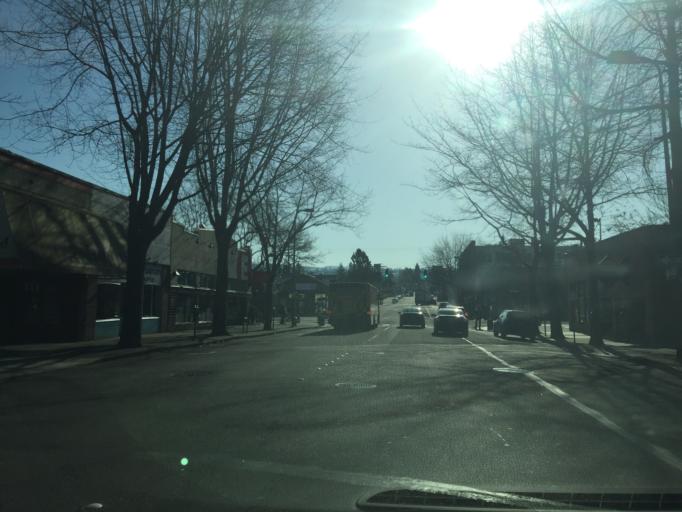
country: US
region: Washington
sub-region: Whatcom County
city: Bellingham
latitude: 48.7506
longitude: -122.4773
